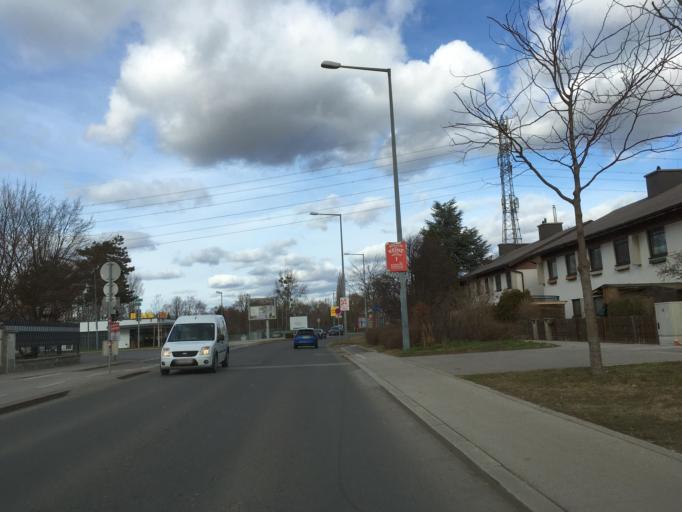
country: AT
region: Lower Austria
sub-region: Politischer Bezirk Ganserndorf
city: Gross-Enzersdorf
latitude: 48.2122
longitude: 16.4792
